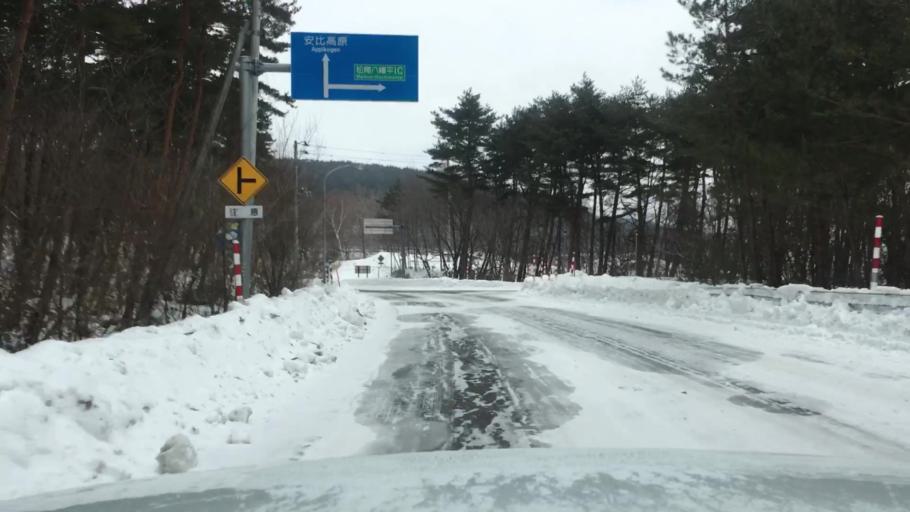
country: JP
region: Iwate
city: Shizukuishi
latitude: 39.9476
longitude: 140.9985
